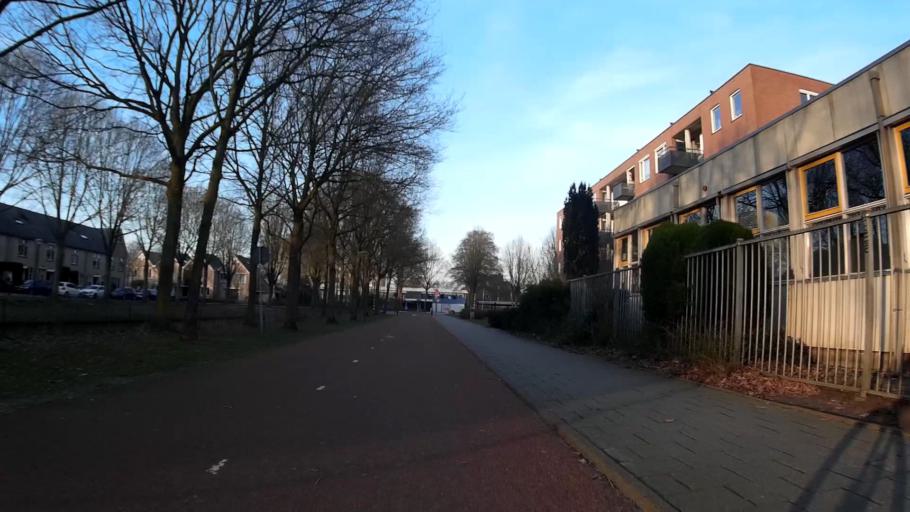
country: NL
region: Utrecht
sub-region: Gemeente Veenendaal
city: Veenendaal
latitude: 52.0270
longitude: 5.5305
